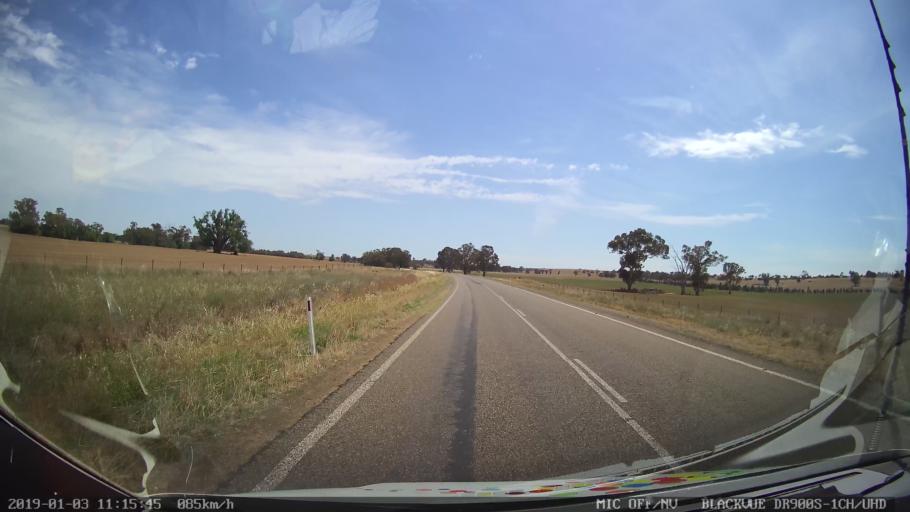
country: AU
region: New South Wales
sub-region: Young
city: Young
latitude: -34.1604
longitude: 148.2673
